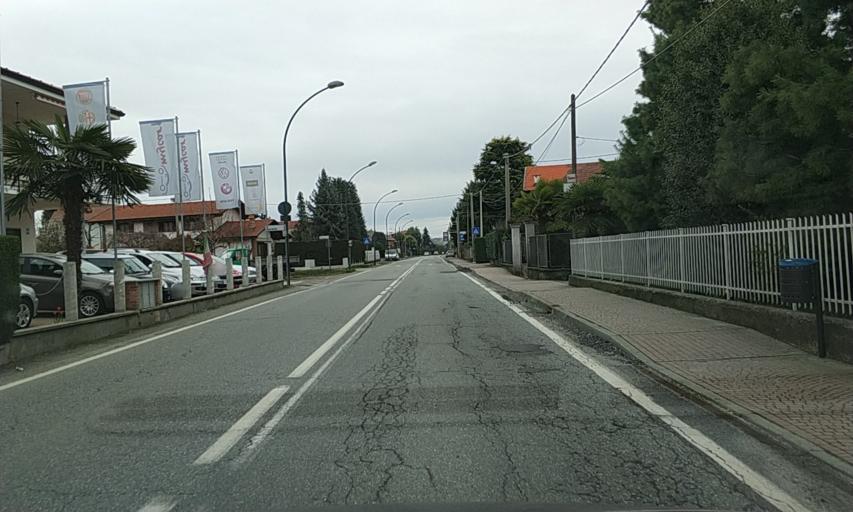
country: IT
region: Piedmont
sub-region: Provincia di Torino
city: Favria
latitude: 45.3315
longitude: 7.6980
